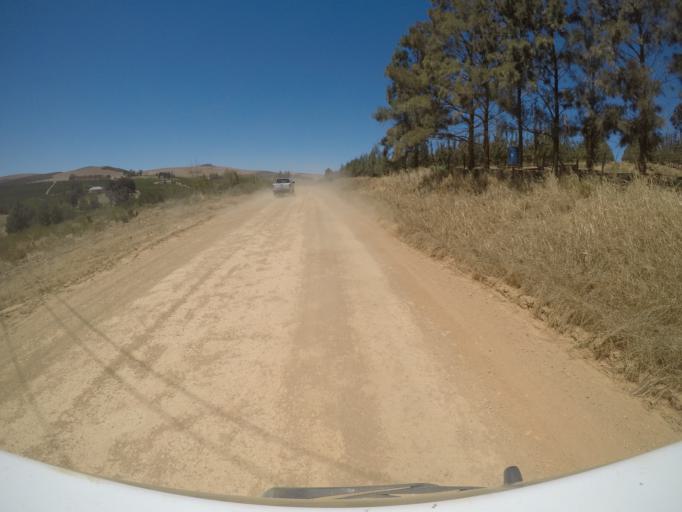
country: ZA
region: Western Cape
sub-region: Overberg District Municipality
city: Grabouw
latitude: -34.0914
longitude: 19.1927
